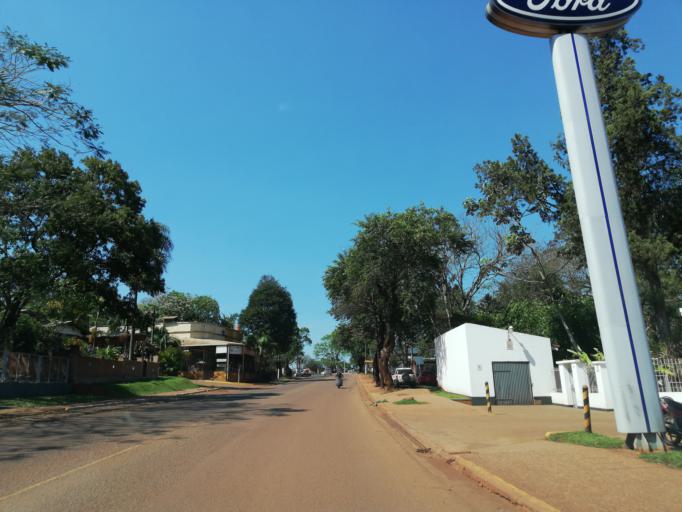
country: AR
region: Misiones
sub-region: Departamento de Eldorado
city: Eldorado
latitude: -26.4072
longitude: -54.6470
